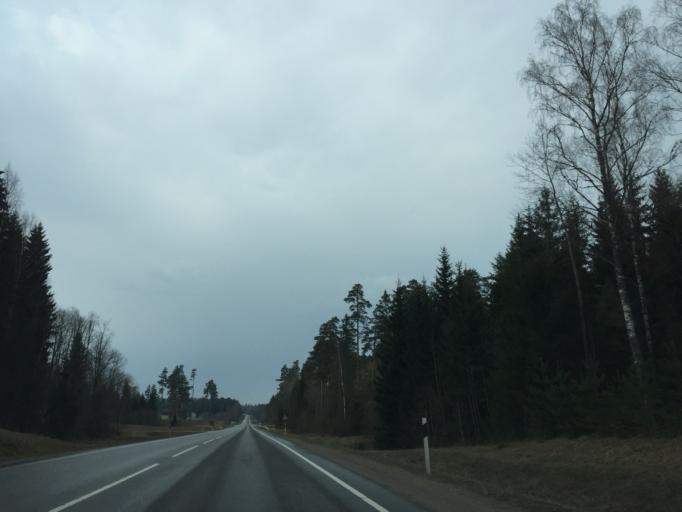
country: EE
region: Tartu
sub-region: UElenurme vald
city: Ulenurme
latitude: 58.1075
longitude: 26.7385
